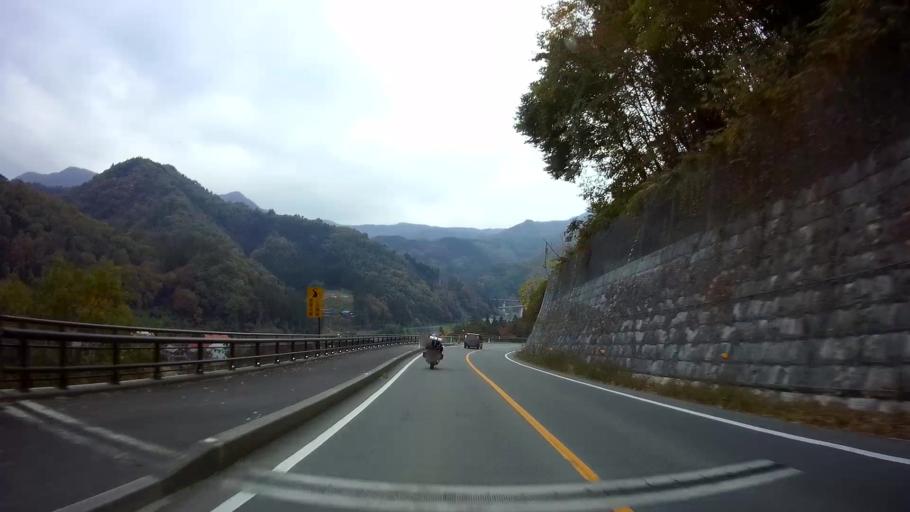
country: JP
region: Gunma
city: Nakanojomachi
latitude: 36.5651
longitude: 138.7299
